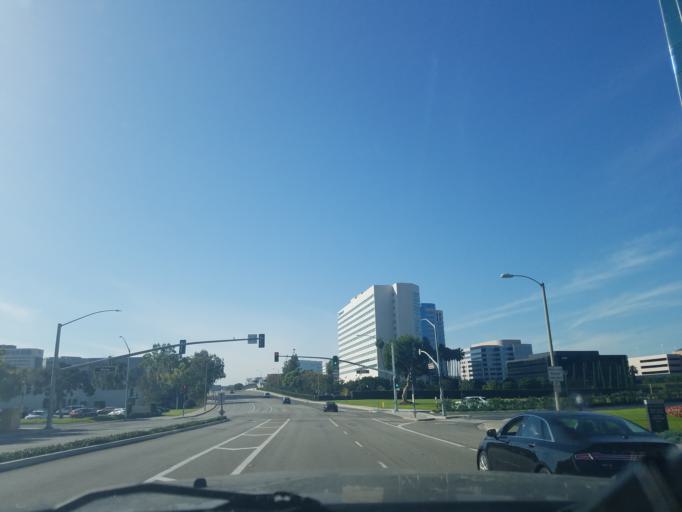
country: US
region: California
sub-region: Orange County
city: Irvine
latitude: 33.6830
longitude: -117.8489
